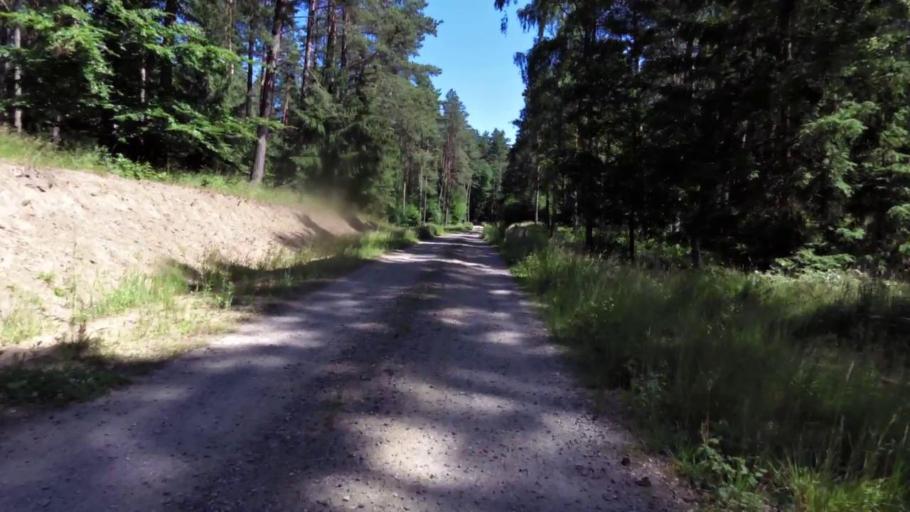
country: PL
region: West Pomeranian Voivodeship
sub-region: Powiat swidwinski
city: Rabino
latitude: 53.8595
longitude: 16.0326
